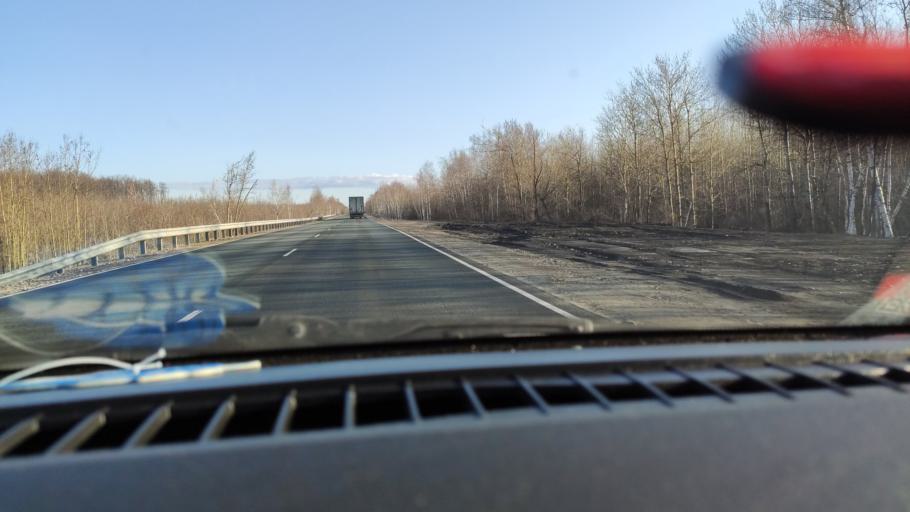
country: RU
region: Saratov
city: Khvalynsk
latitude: 52.4238
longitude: 48.0084
